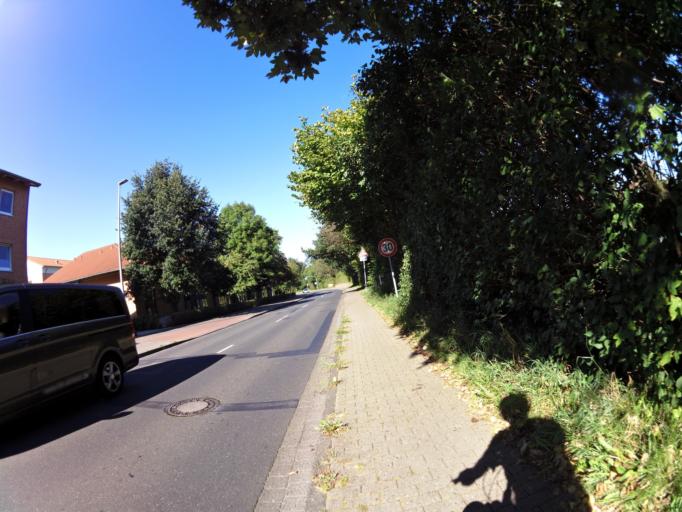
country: DE
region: Schleswig-Holstein
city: Barkelsby
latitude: 54.4866
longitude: 9.8257
